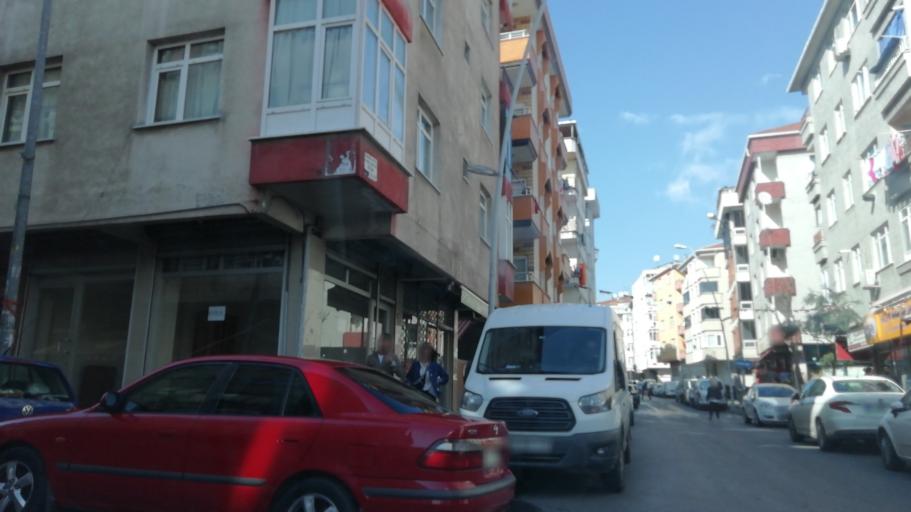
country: TR
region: Istanbul
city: Bahcelievler
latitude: 40.9961
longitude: 28.8369
